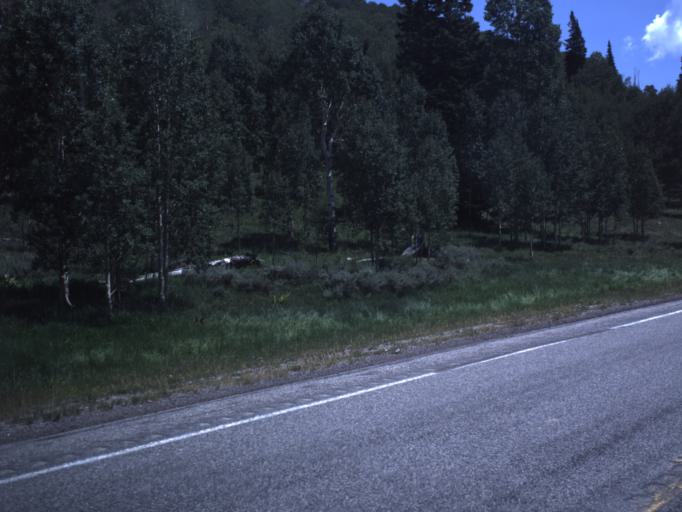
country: US
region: Utah
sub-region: Sanpete County
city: Fairview
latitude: 39.5861
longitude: -111.2386
